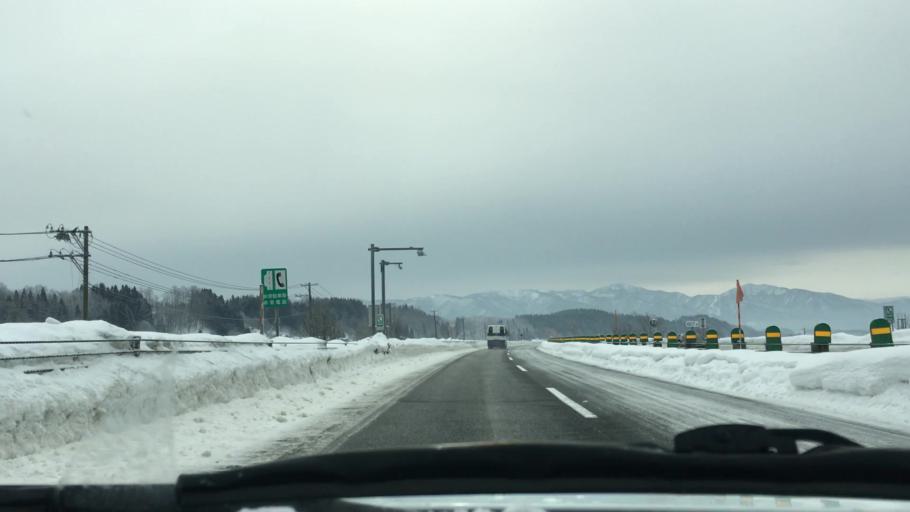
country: JP
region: Akita
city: Hanawa
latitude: 40.2962
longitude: 140.7537
